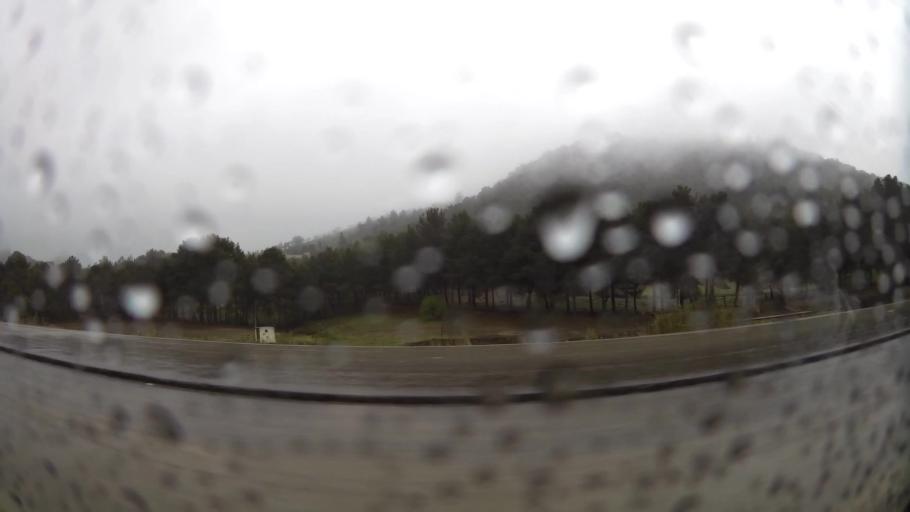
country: MA
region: Taza-Al Hoceima-Taounate
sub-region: Taza
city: Aknoul
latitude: 34.7558
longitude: -3.8041
